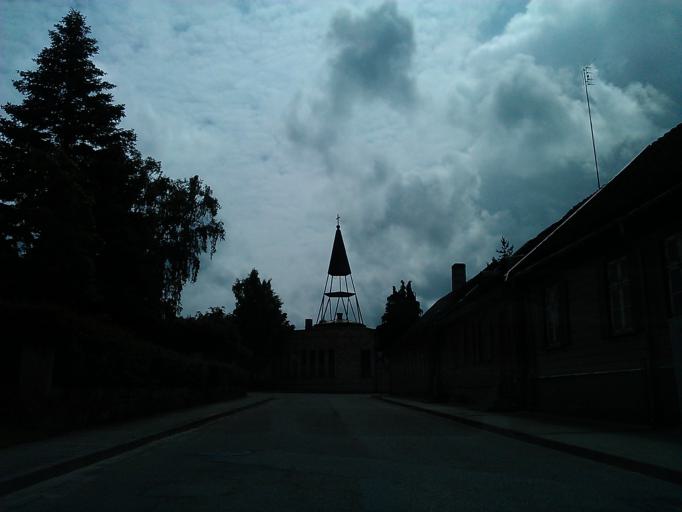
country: LV
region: Aizpute
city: Aizpute
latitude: 56.7224
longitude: 21.6052
